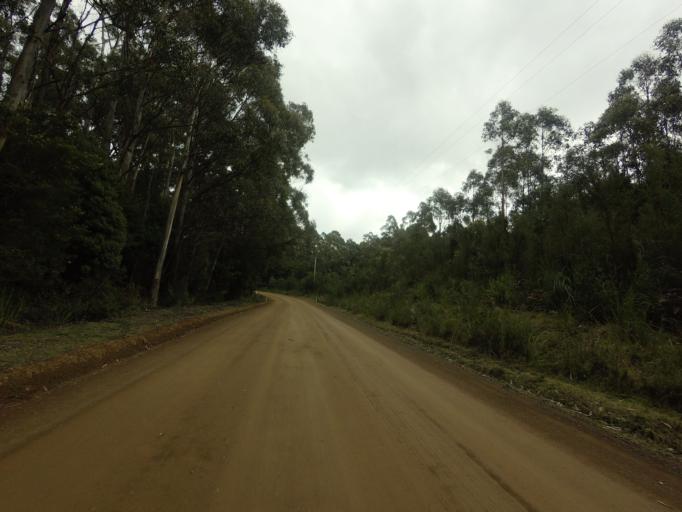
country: AU
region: Tasmania
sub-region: Huon Valley
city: Geeveston
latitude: -43.4136
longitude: 146.9039
